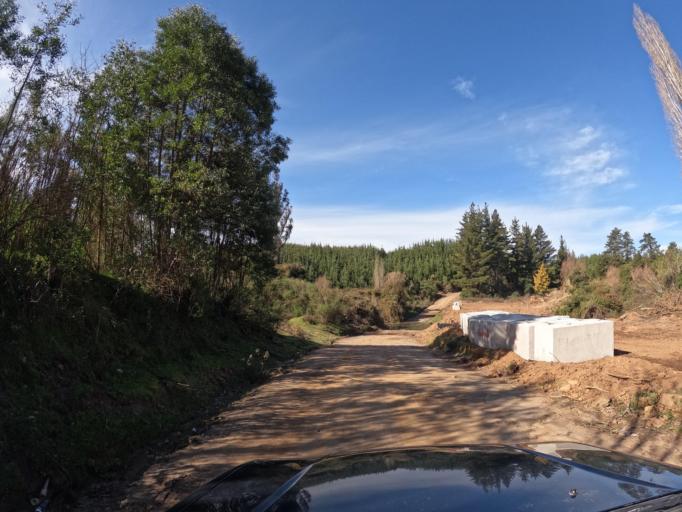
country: CL
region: Biobio
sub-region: Provincia de Biobio
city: La Laja
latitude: -37.0880
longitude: -72.7758
